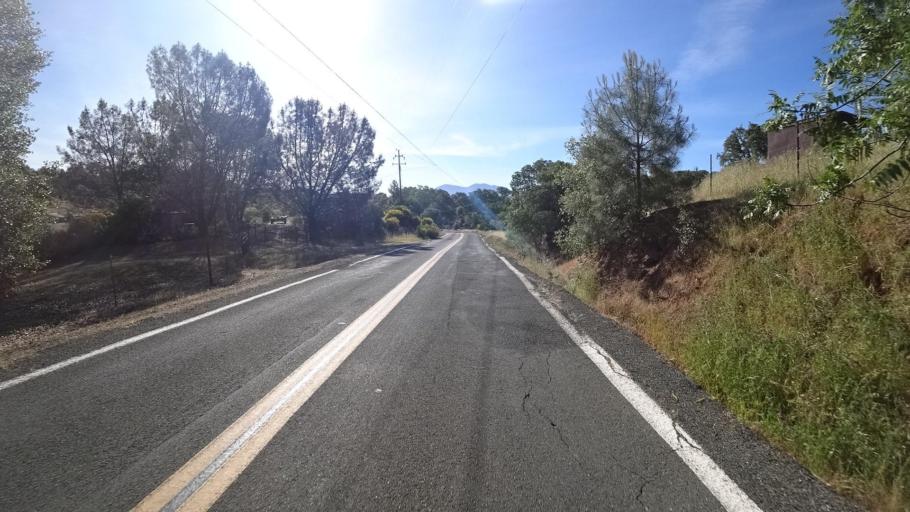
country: US
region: California
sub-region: Lake County
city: Lakeport
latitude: 39.0411
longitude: -122.9443
